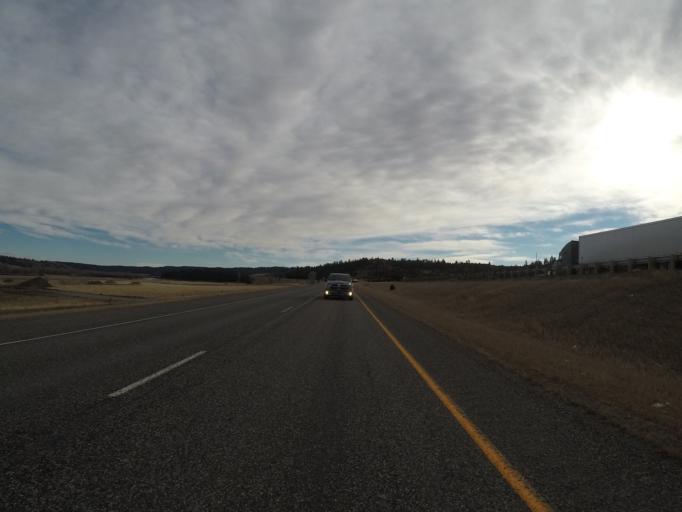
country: US
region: Montana
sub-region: Stillwater County
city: Absarokee
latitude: 45.6958
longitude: -109.4875
